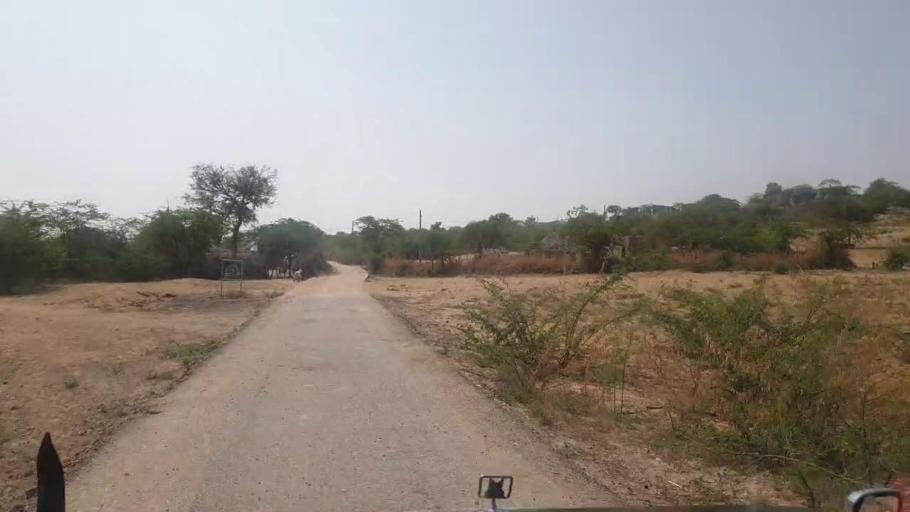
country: PK
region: Sindh
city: Islamkot
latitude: 25.1257
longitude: 70.2175
